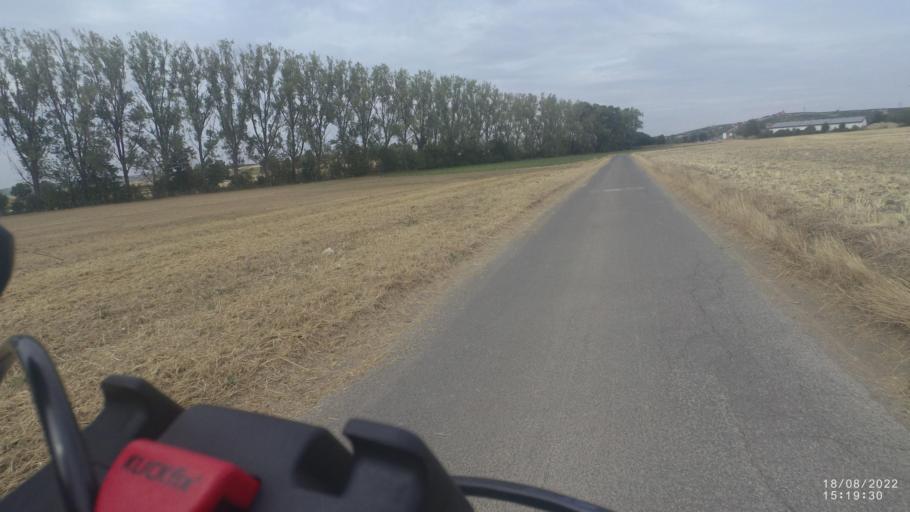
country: DE
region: Rheinland-Pfalz
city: Sulzheim
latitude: 49.8385
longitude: 8.0827
